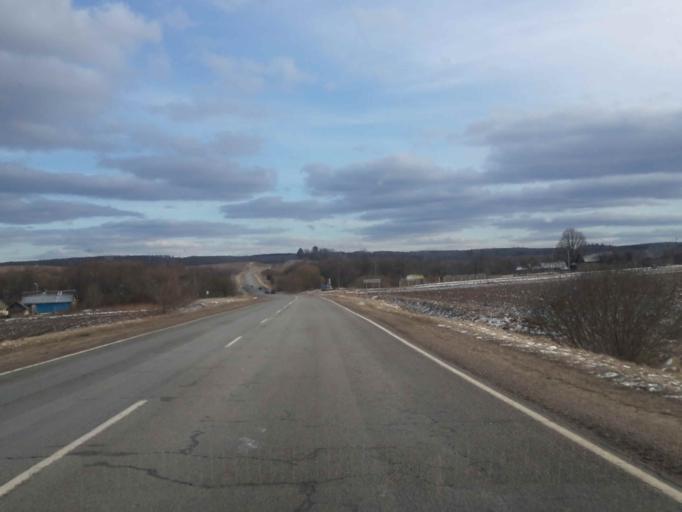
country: BY
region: Minsk
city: Il'ya
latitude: 54.3008
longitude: 27.4771
